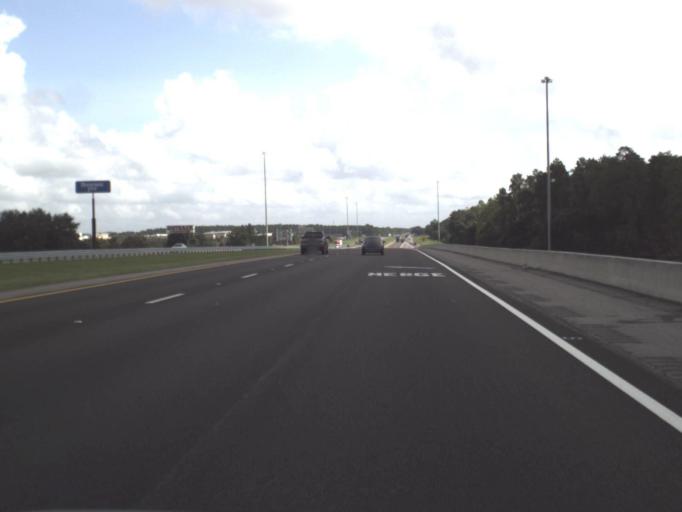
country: US
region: Florida
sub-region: Pasco County
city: Wesley Chapel
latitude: 28.2372
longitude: -82.3539
